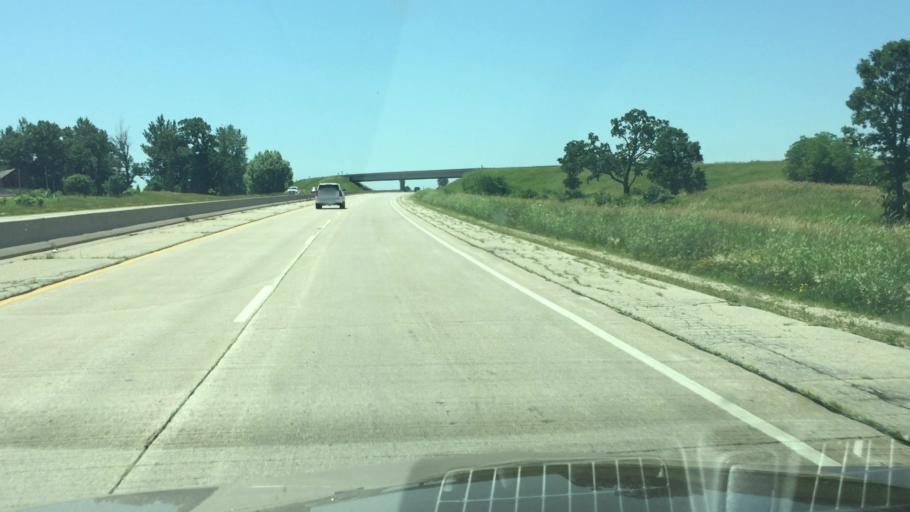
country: US
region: Wisconsin
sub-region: Fond du Lac County
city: Waupun
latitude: 43.5861
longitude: -88.7473
